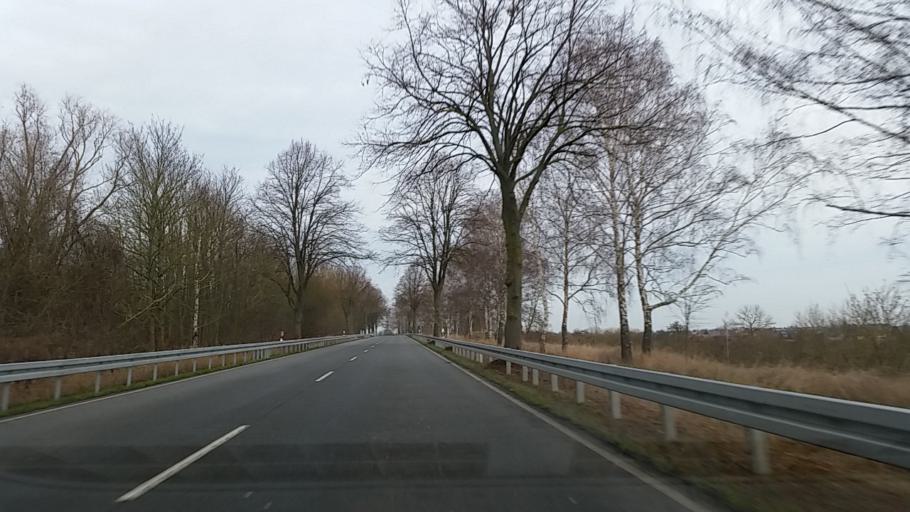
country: DE
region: Lower Saxony
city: Cramme
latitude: 52.1287
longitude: 10.4312
